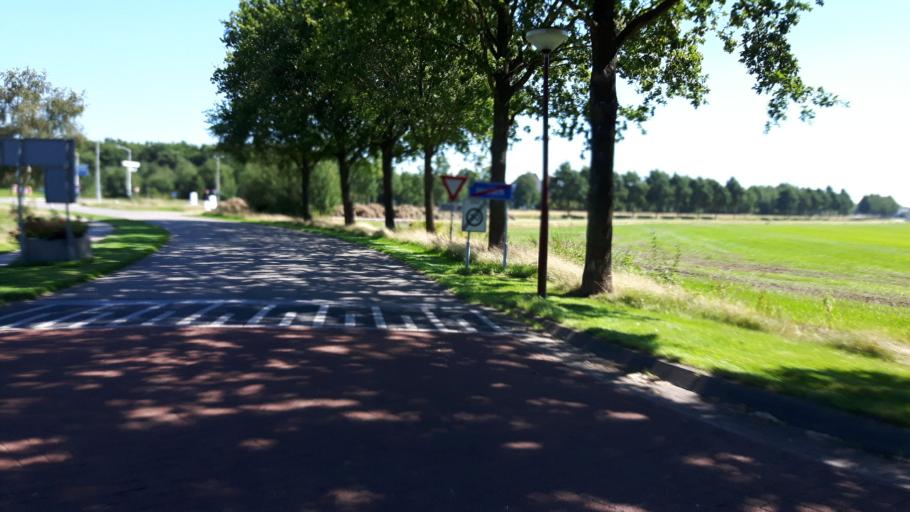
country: NL
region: Friesland
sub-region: Gemeente Gaasterlan-Sleat
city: Balk
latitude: 52.9024
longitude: 5.5668
